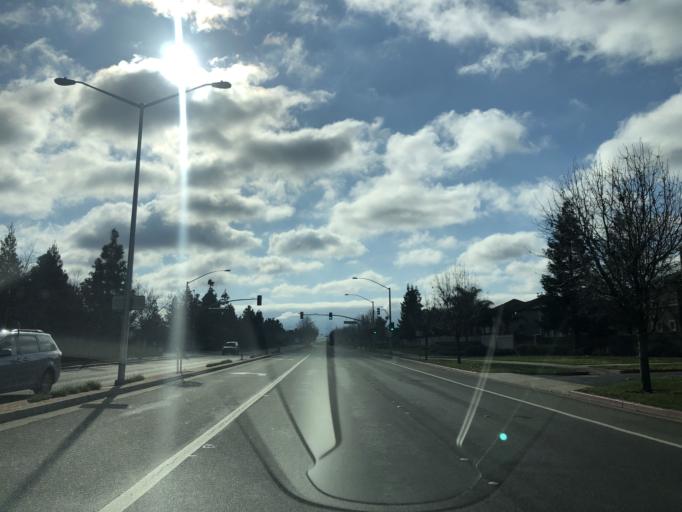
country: US
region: California
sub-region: Contra Costa County
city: Oakley
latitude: 37.9607
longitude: -121.7509
